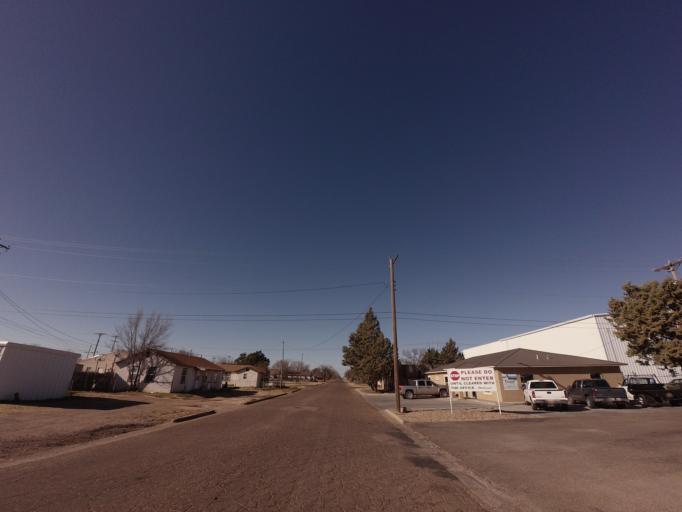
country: US
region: New Mexico
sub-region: Curry County
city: Clovis
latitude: 34.4018
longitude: -103.1881
